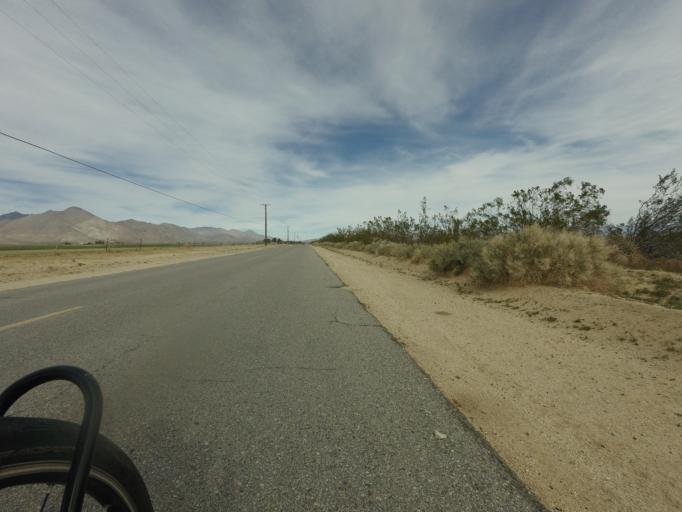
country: US
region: California
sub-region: Kern County
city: Inyokern
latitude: 35.7403
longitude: -117.8400
